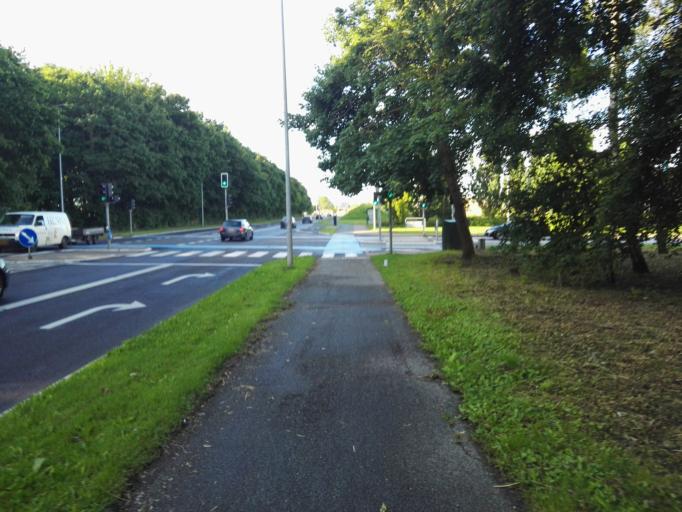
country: DK
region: Capital Region
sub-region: Egedal Kommune
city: Smorumnedre
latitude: 55.7324
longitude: 12.3098
